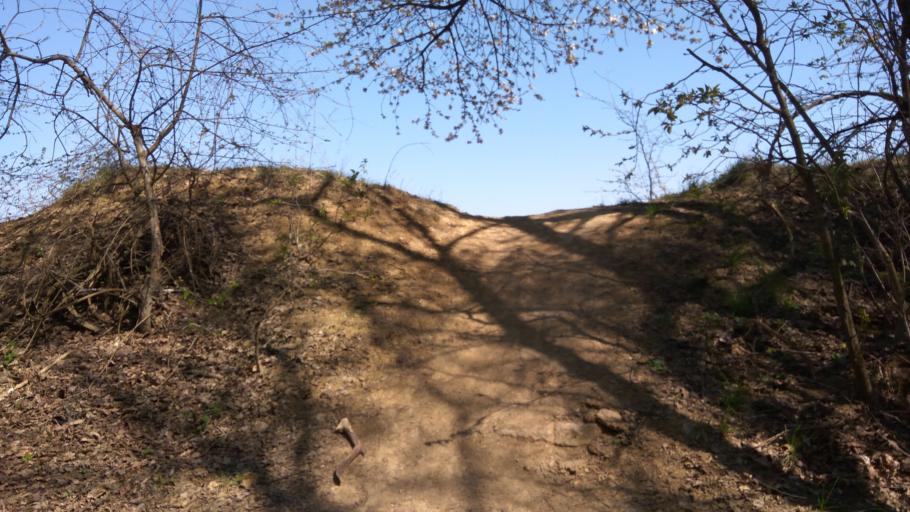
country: HU
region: Pest
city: Pilisborosjeno
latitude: 47.6208
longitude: 19.0064
